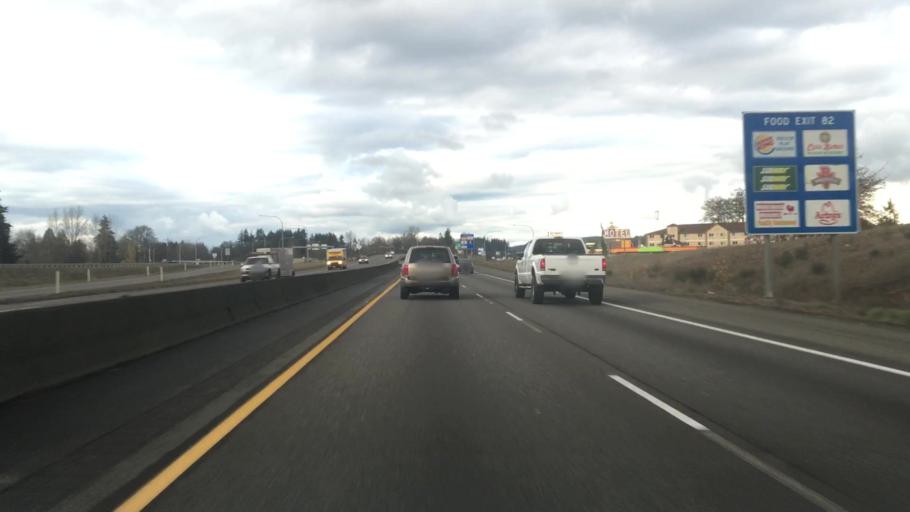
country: US
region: Washington
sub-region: Lewis County
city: Centralia
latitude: 46.7071
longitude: -122.9750
